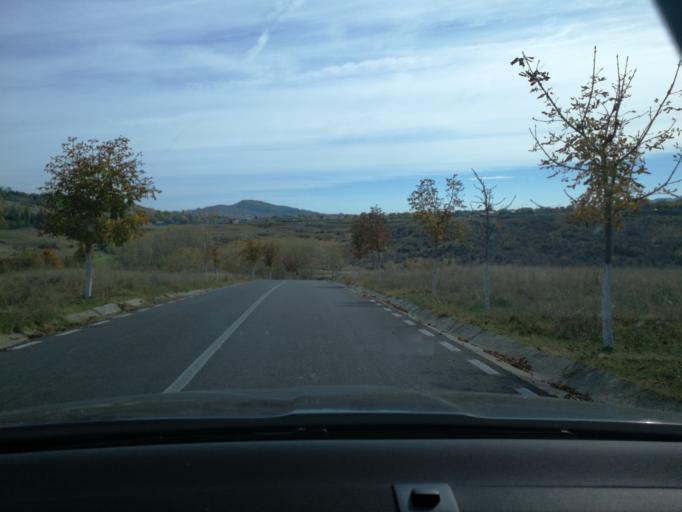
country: RO
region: Prahova
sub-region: Comuna Cornu
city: Cornu de Jos
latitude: 45.1503
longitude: 25.7233
